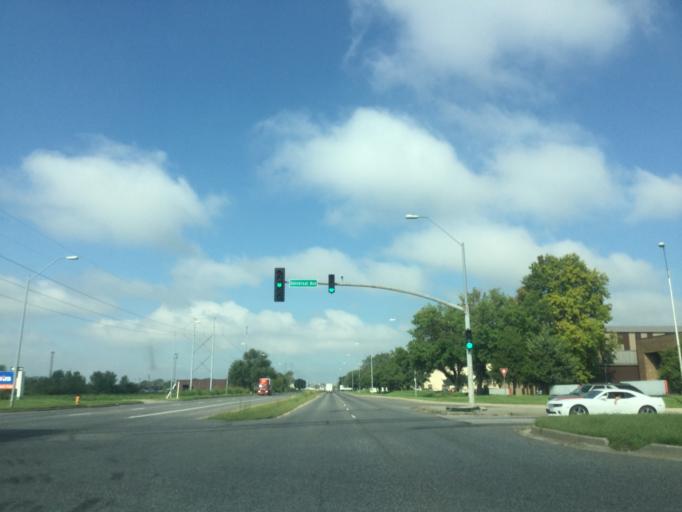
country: US
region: Missouri
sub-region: Clay County
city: North Kansas City
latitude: 39.1304
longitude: -94.5060
